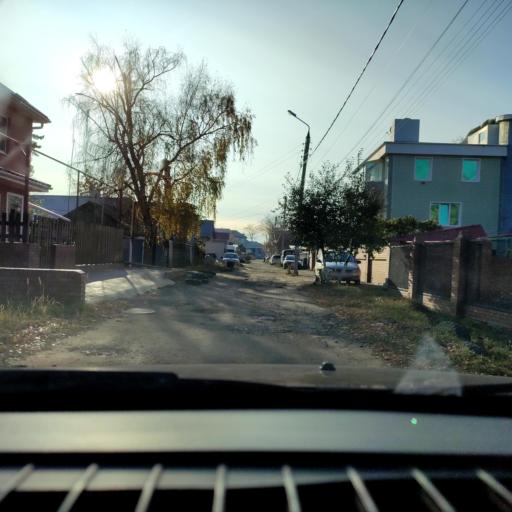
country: RU
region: Samara
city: Tol'yatti
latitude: 53.5197
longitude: 49.4092
